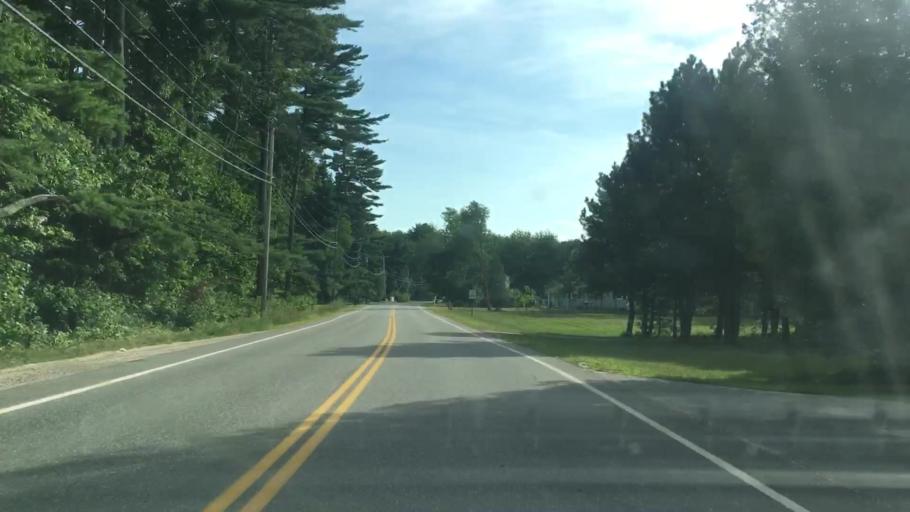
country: US
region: Maine
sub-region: Cumberland County
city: Brunswick
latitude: 43.9254
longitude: -69.8955
